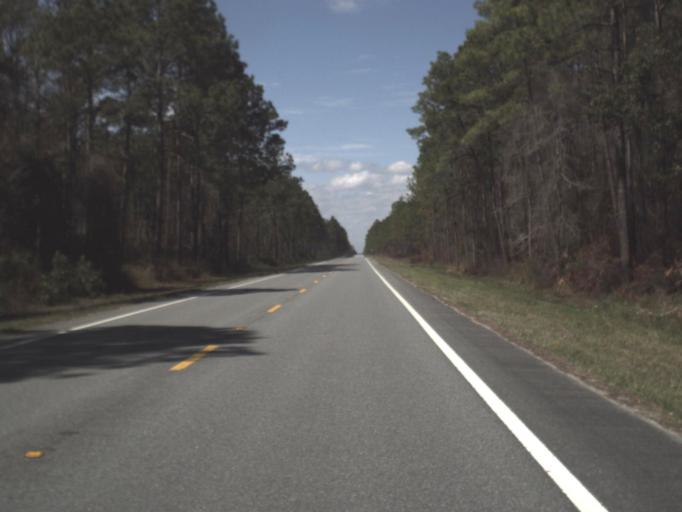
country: US
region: Florida
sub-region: Gadsden County
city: Midway
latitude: 30.3615
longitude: -84.5350
